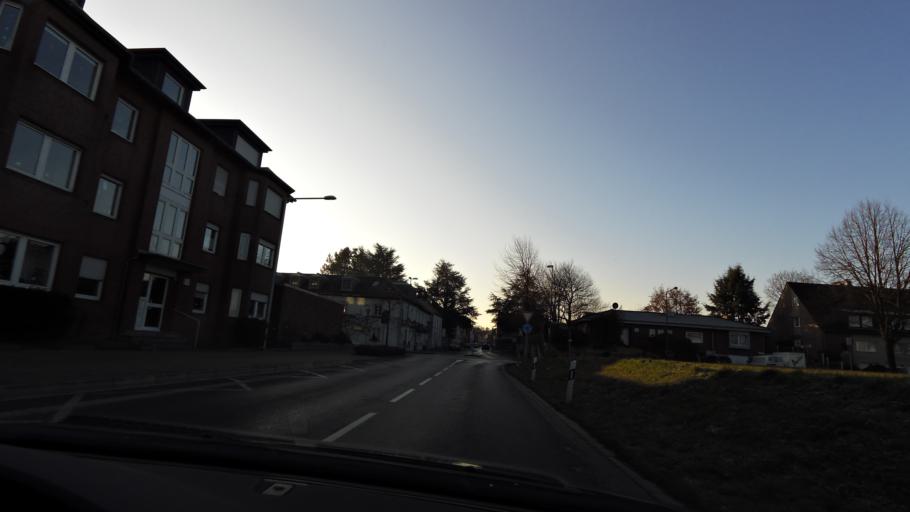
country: NL
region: Limburg
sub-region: Gemeente Kerkrade
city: Kerkrade
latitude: 50.8180
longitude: 6.0569
